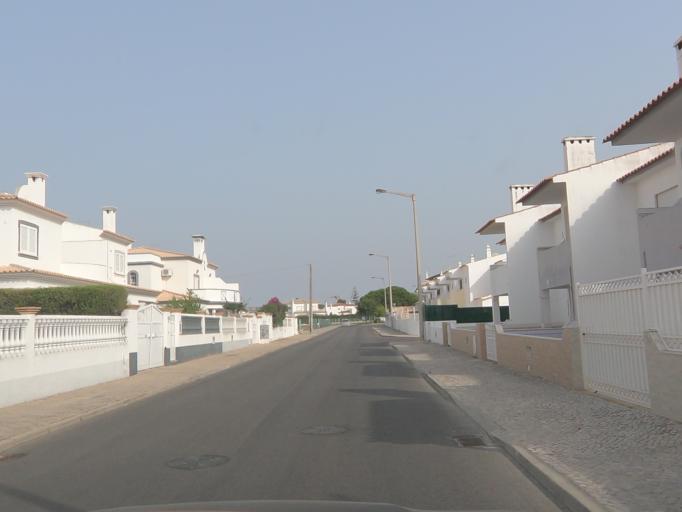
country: PT
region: Faro
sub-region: Albufeira
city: Guia
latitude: 37.0825
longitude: -8.3092
